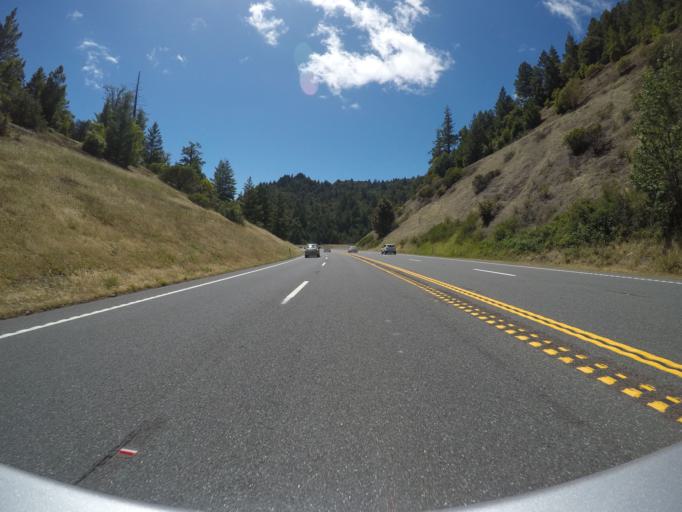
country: US
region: California
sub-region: Mendocino County
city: Laytonville
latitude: 39.8331
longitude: -123.6461
